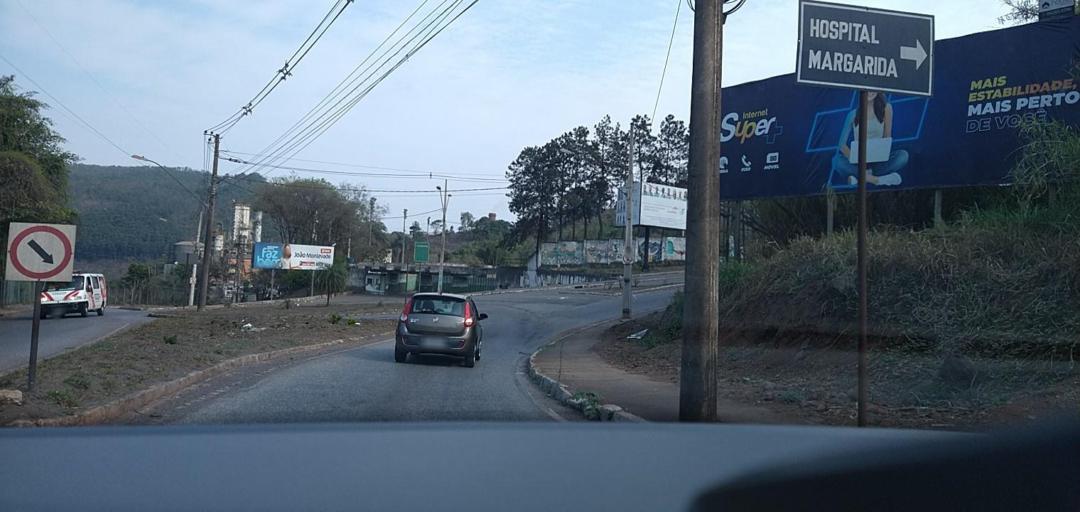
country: BR
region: Minas Gerais
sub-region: Joao Monlevade
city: Joao Monlevade
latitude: -19.8205
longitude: -43.1332
